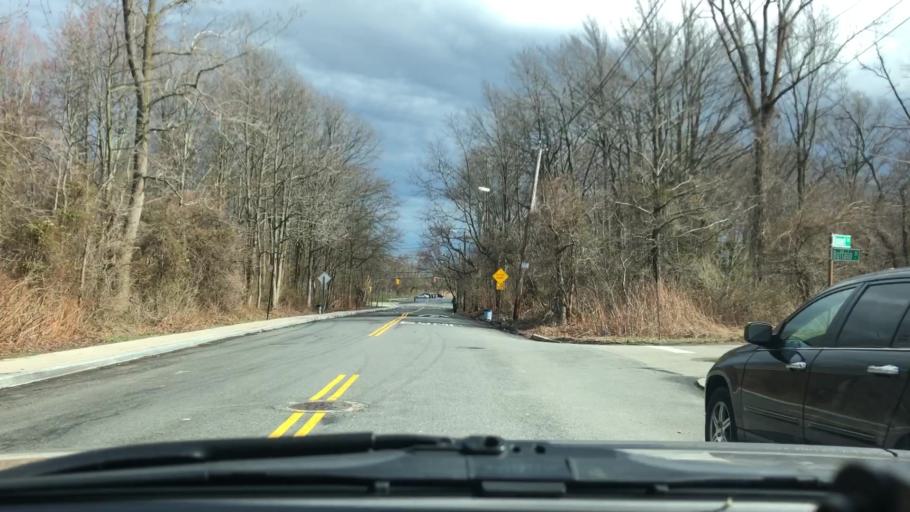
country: US
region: New York
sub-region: Richmond County
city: Staten Island
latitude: 40.5576
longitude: -74.1298
